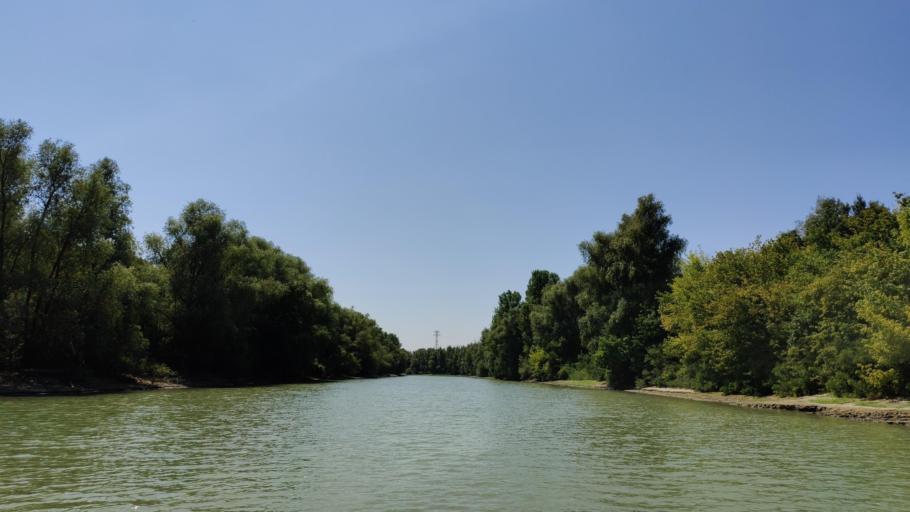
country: RO
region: Tulcea
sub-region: Municipiul Tulcea
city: Tulcea
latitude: 45.2096
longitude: 28.8577
